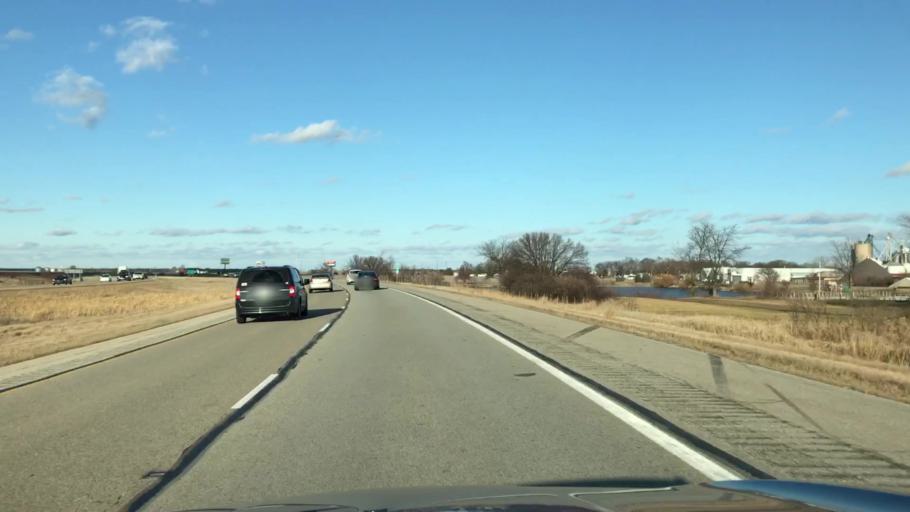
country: US
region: Illinois
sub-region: McLean County
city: Hudson
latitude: 40.5580
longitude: -88.9099
